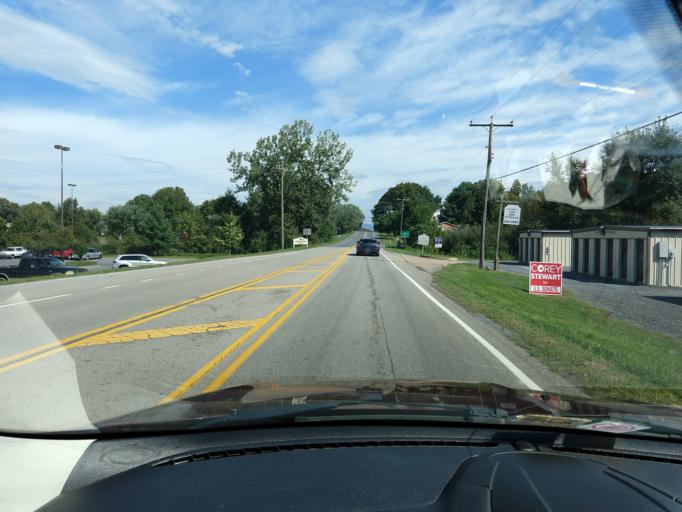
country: US
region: Virginia
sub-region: Rockingham County
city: Grottoes
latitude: 38.2588
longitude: -78.8209
